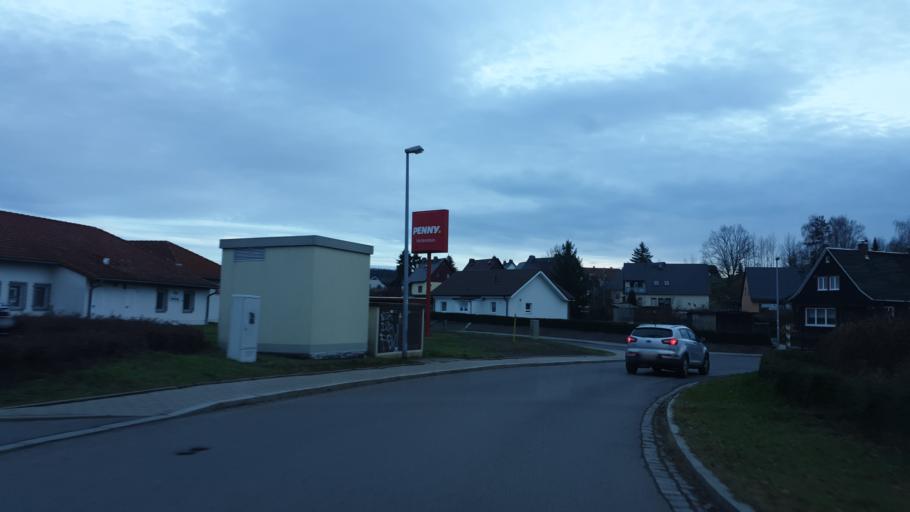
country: DE
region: Saxony
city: Hartenstein
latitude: 50.6674
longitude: 12.6687
